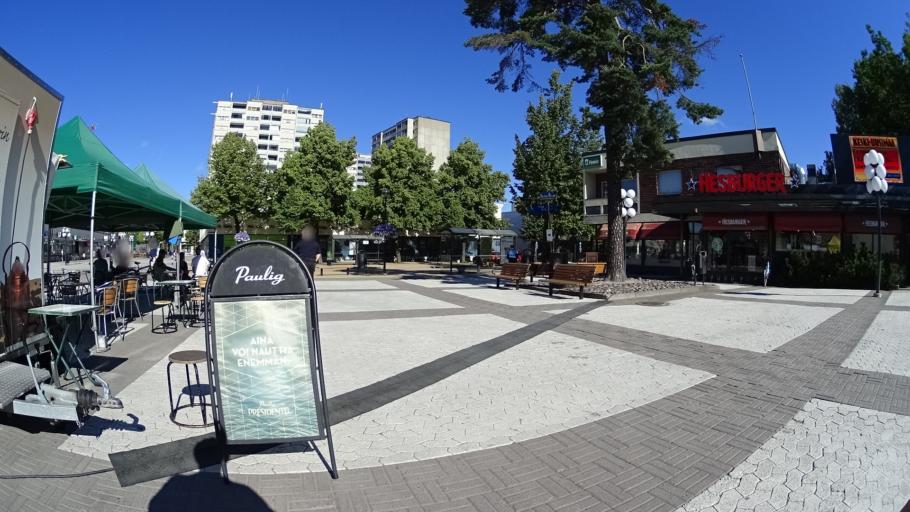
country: FI
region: Uusimaa
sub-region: Helsinki
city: Kerava
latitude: 60.4032
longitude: 25.1016
